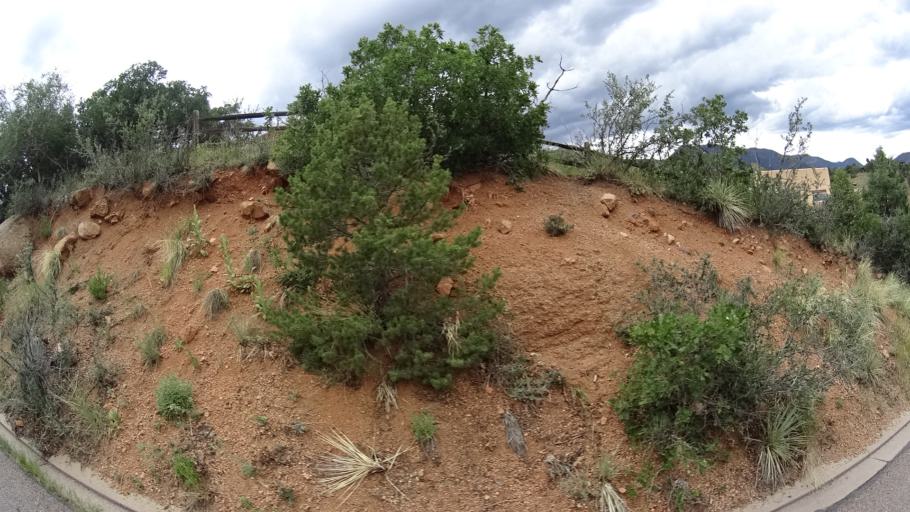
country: US
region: Colorado
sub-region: El Paso County
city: Manitou Springs
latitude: 38.8463
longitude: -104.8969
